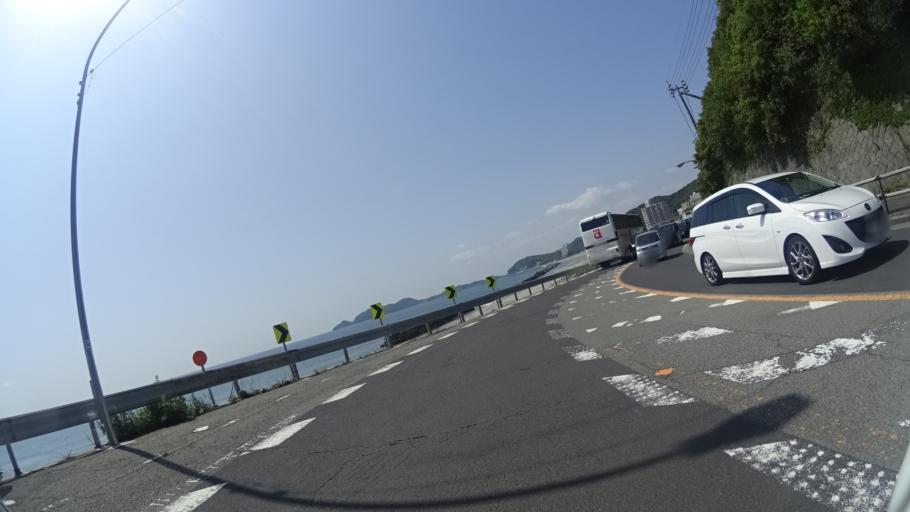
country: JP
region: Tokushima
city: Narutocho-mitsuishi
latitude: 34.2139
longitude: 134.6300
